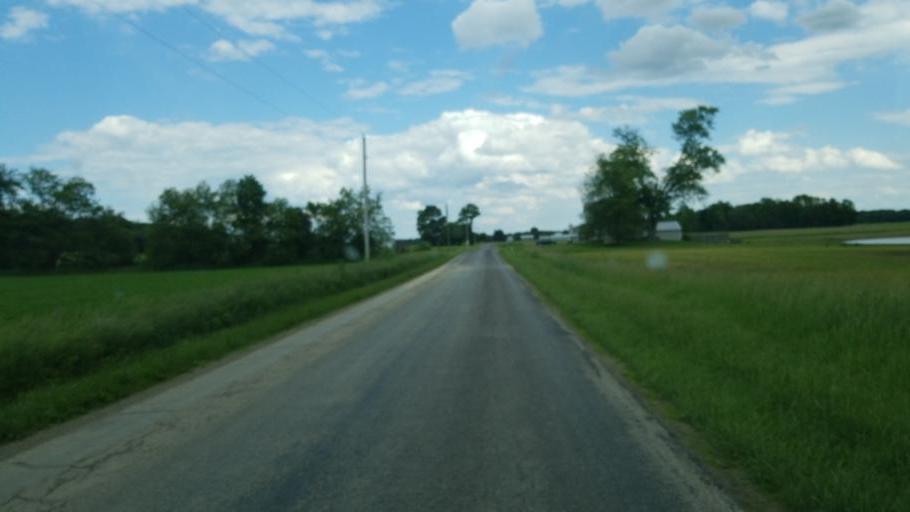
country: US
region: Ohio
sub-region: Huron County
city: Plymouth
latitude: 40.9451
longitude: -82.6365
